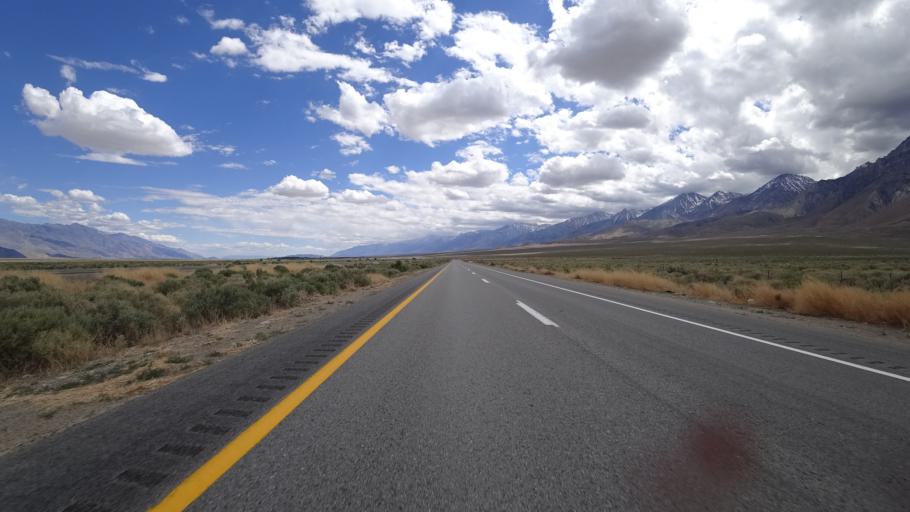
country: US
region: California
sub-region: Inyo County
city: Big Pine
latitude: 36.9006
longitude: -118.2420
